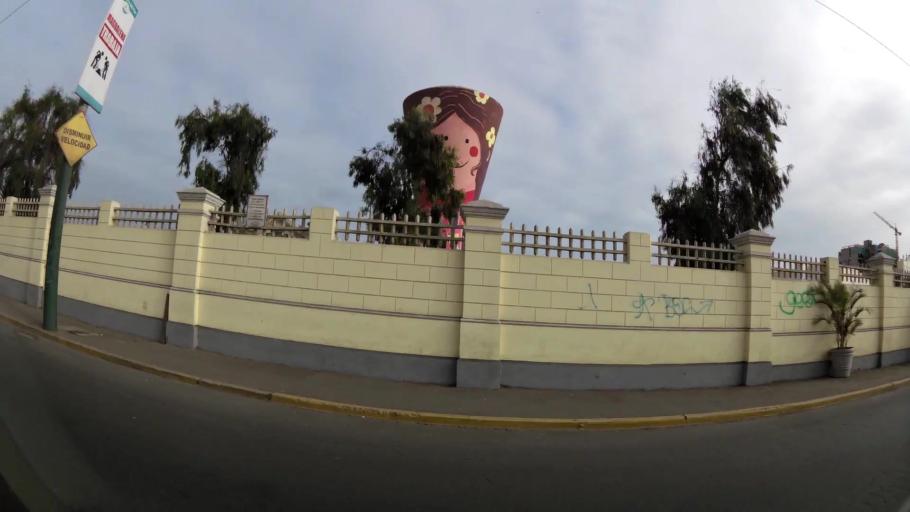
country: PE
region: Lima
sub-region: Lima
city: San Isidro
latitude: -12.0990
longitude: -77.0669
